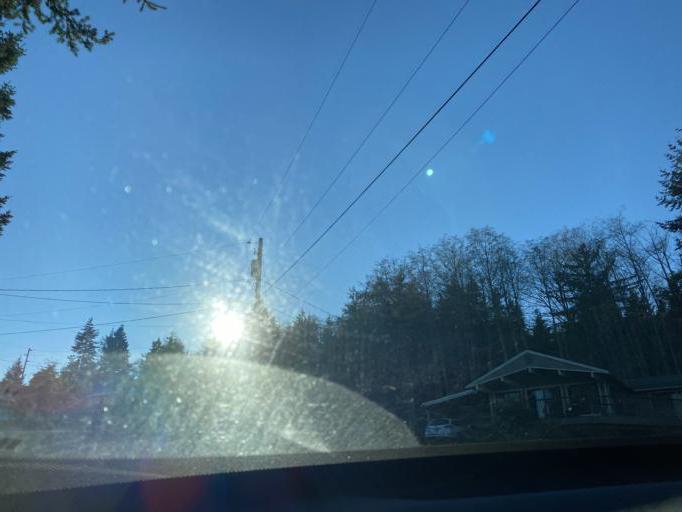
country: US
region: Washington
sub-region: Island County
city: Camano
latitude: 48.1299
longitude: -122.5669
